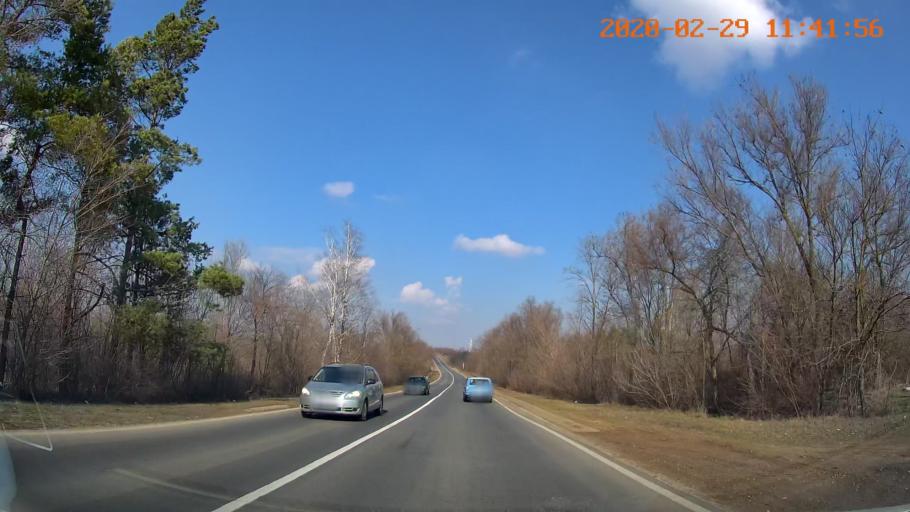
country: MD
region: Rezina
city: Saharna
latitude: 47.6777
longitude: 29.0149
